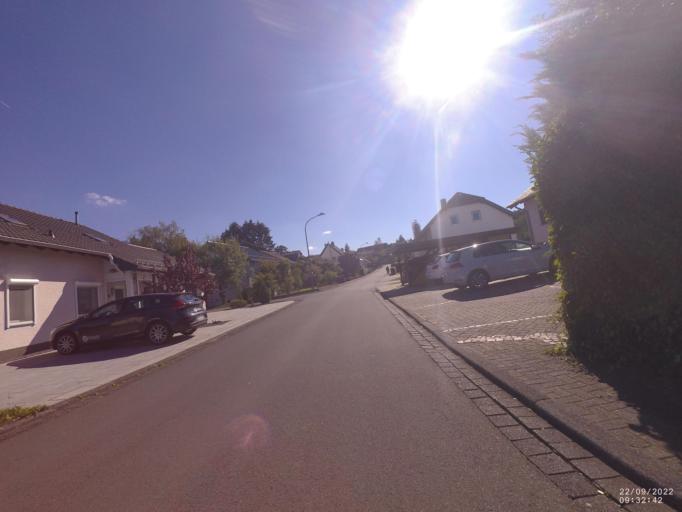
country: DE
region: Rheinland-Pfalz
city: Walsdorf
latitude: 50.2815
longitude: 6.7109
